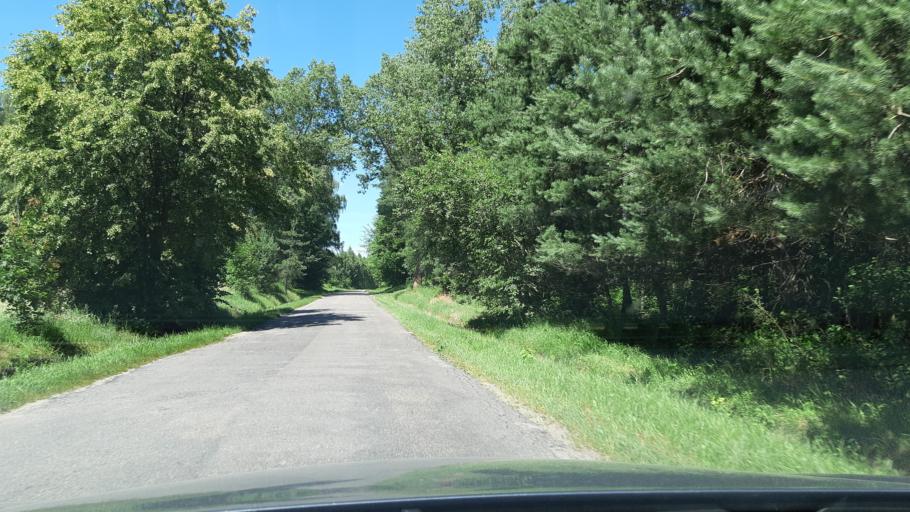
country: PL
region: Warmian-Masurian Voivodeship
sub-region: Powiat gizycki
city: Gizycko
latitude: 53.9539
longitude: 21.7613
